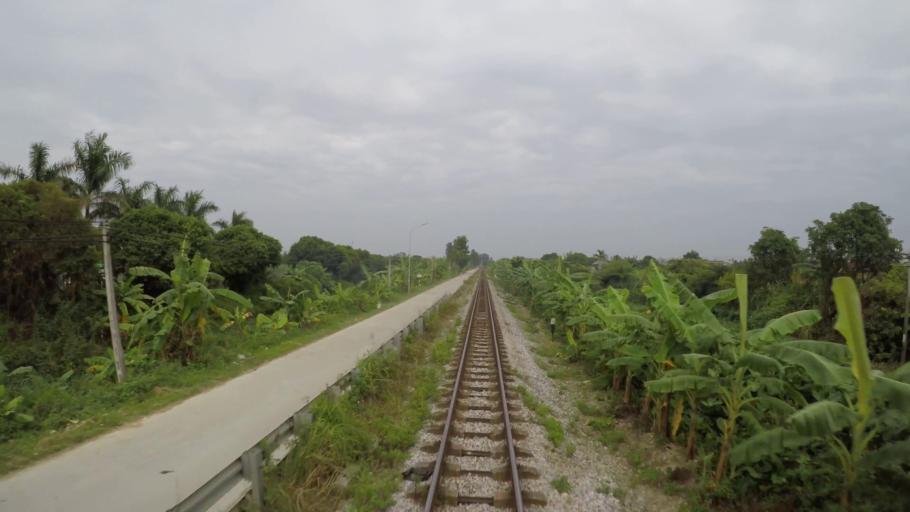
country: VN
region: Hai Duong
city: Lai Cach
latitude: 20.9499
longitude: 106.2453
